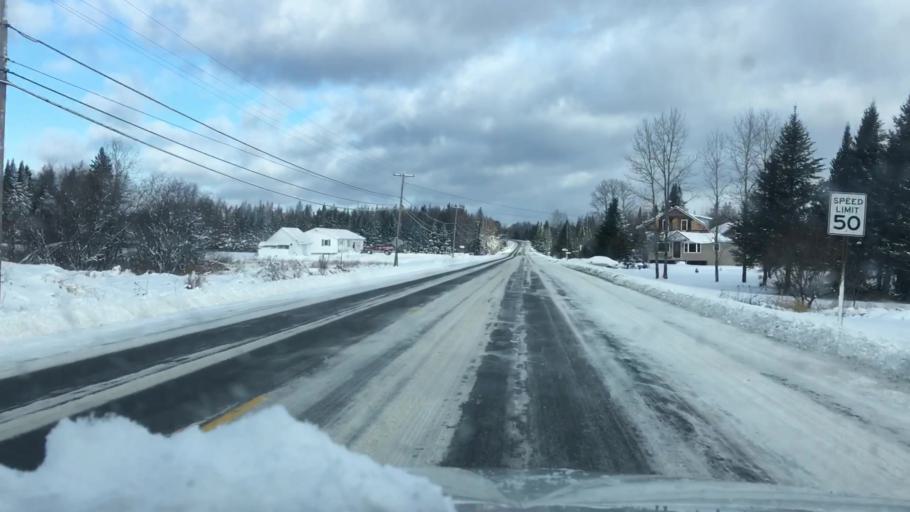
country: US
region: Maine
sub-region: Aroostook County
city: Caribou
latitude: 46.9168
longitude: -68.0187
